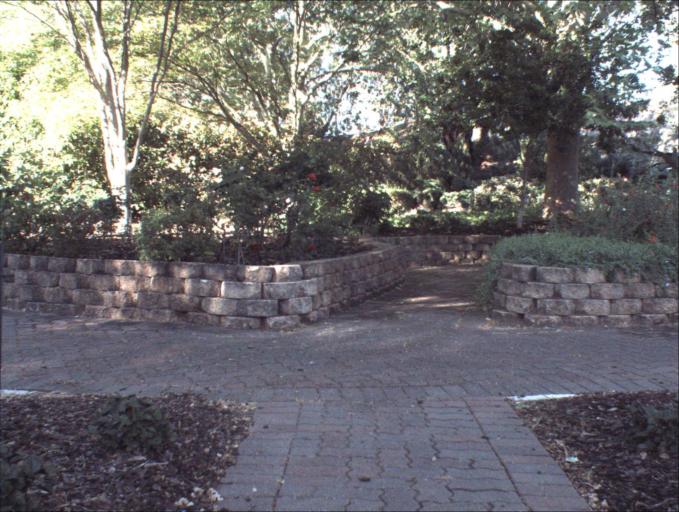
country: AU
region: South Australia
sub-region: Salisbury
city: Ingle Farm
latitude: -34.8412
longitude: 138.6260
